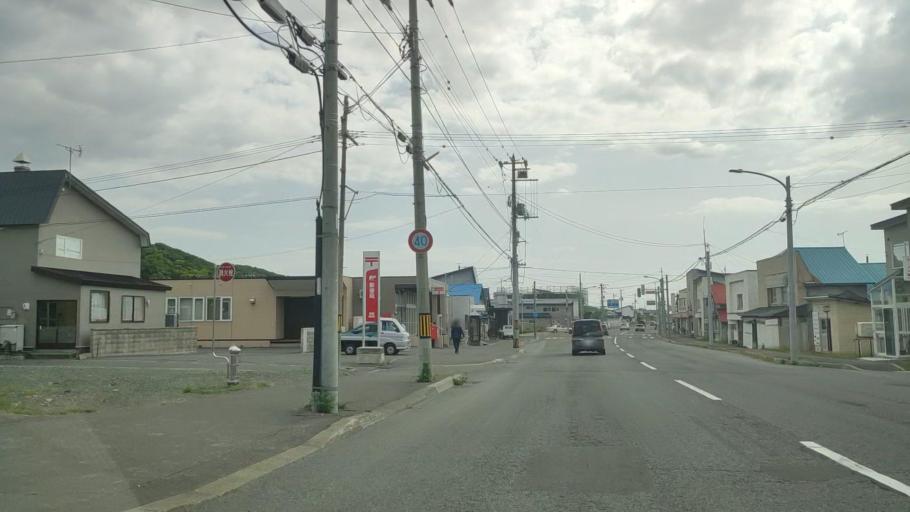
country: JP
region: Hokkaido
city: Rumoi
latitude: 44.1556
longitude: 141.6578
